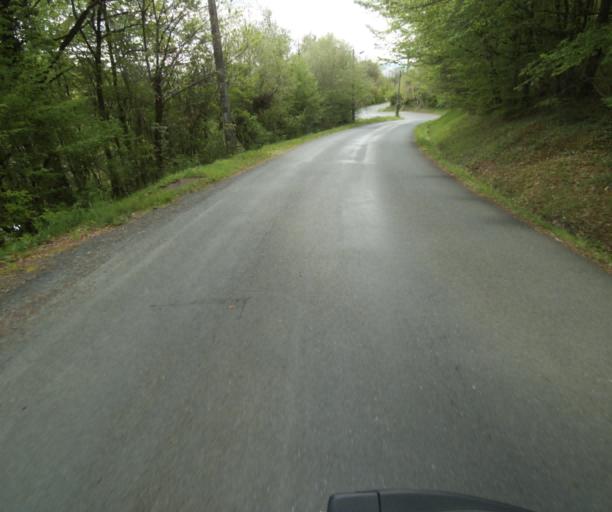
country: FR
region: Limousin
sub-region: Departement de la Correze
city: Tulle
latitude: 45.2838
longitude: 1.7669
